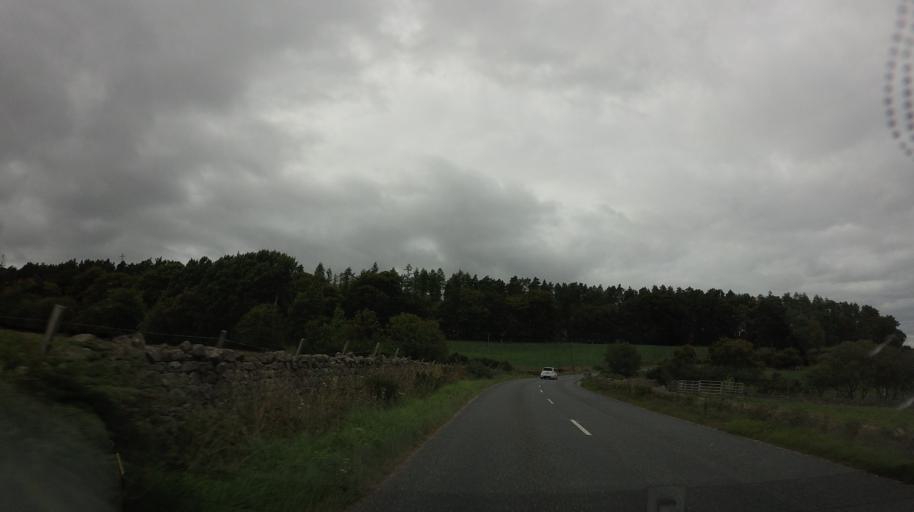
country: GB
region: Scotland
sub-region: Aberdeenshire
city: Banchory
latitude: 57.1188
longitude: -2.4274
